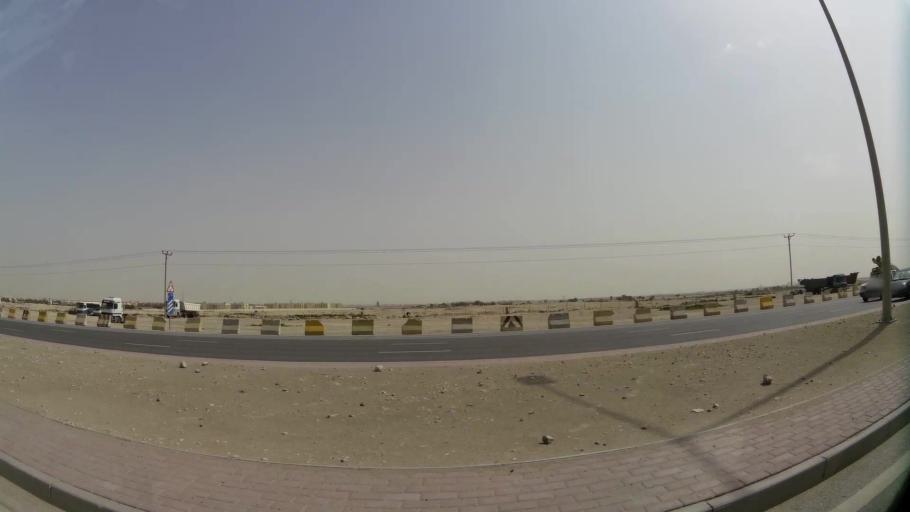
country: QA
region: Baladiyat ar Rayyan
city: Ar Rayyan
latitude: 25.2352
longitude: 51.4012
